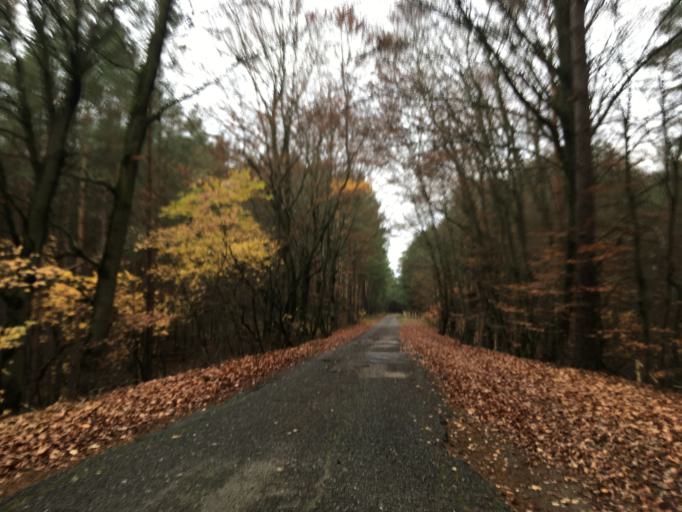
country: DE
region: Brandenburg
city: Jamlitz
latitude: 52.0572
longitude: 14.4809
